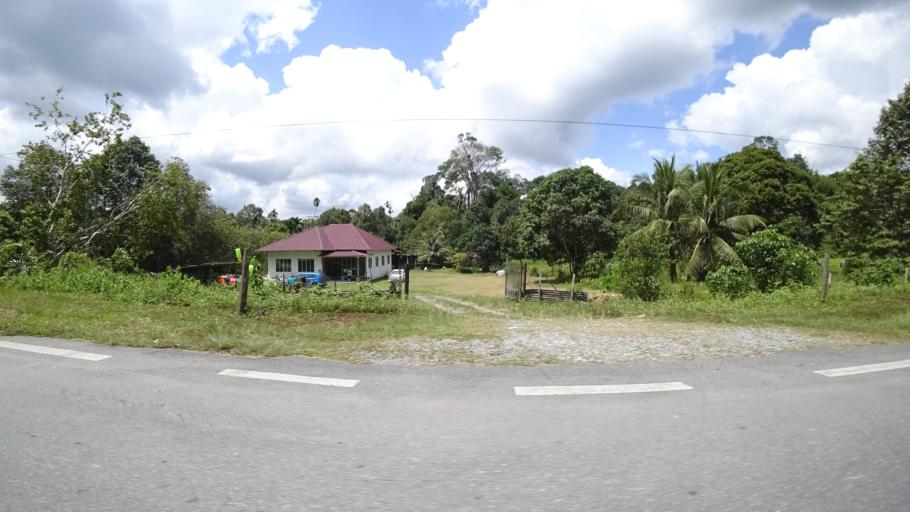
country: BN
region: Tutong
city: Tutong
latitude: 4.7204
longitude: 114.7999
